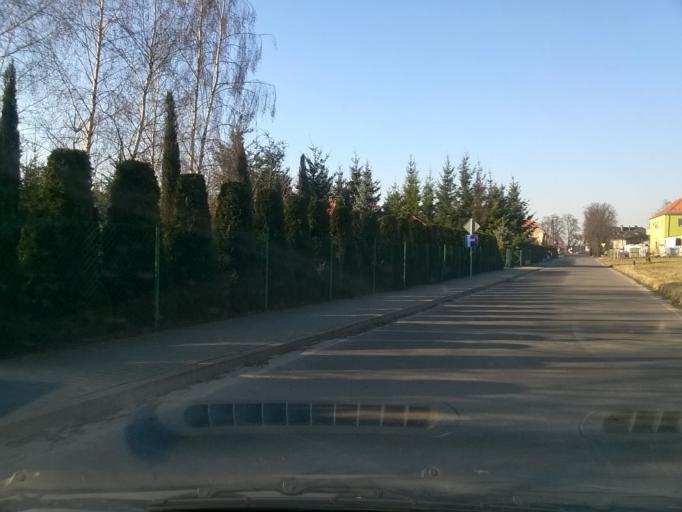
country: PL
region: Greater Poland Voivodeship
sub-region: Powiat wagrowiecki
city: Golancz
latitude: 52.9447
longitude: 17.3063
